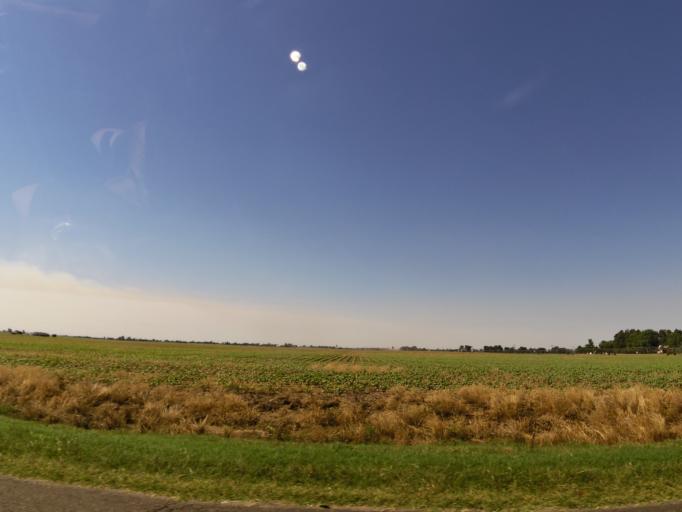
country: US
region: Missouri
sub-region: Dunklin County
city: Campbell
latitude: 36.4921
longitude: -90.0201
